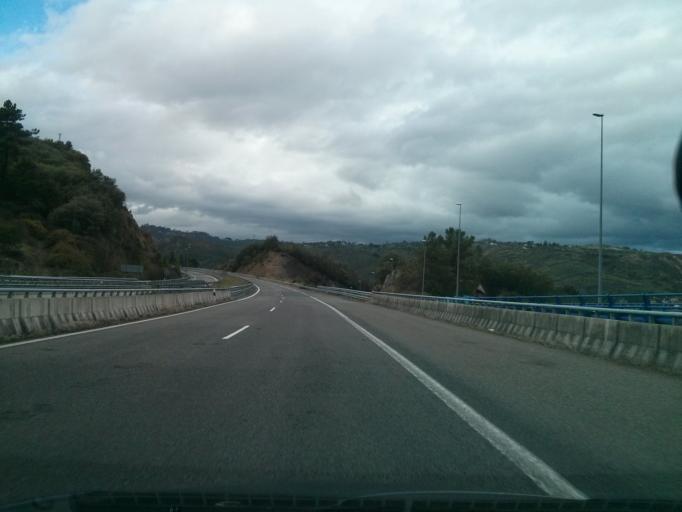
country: ES
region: Galicia
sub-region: Provincia de Ourense
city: Ourense
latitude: 42.3434
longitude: -7.8857
